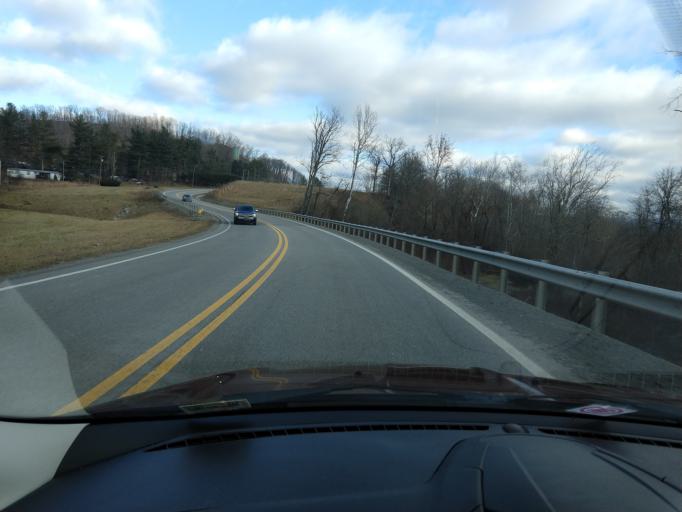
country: US
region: West Virginia
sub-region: Randolph County
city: Elkins
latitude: 38.7853
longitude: -79.9069
